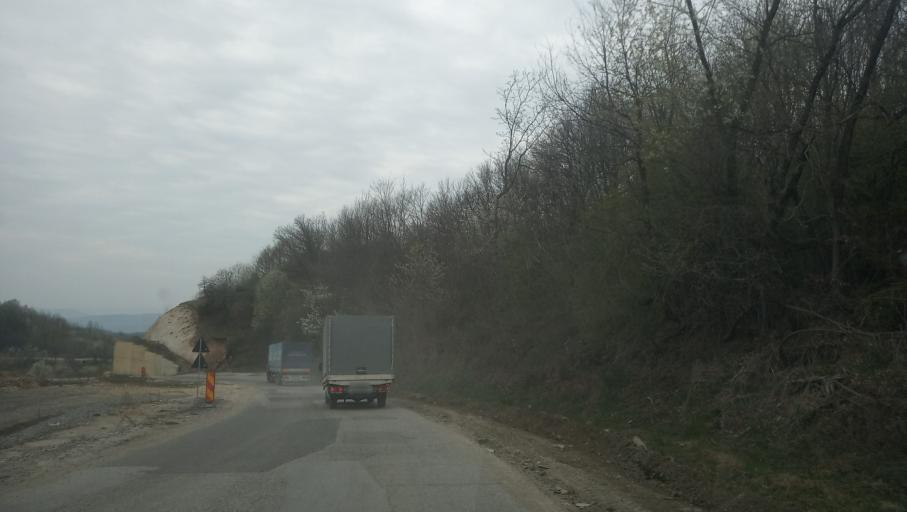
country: RO
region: Arad
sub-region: Comuna Varfurile
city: Varfurile
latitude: 46.3689
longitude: 22.5536
